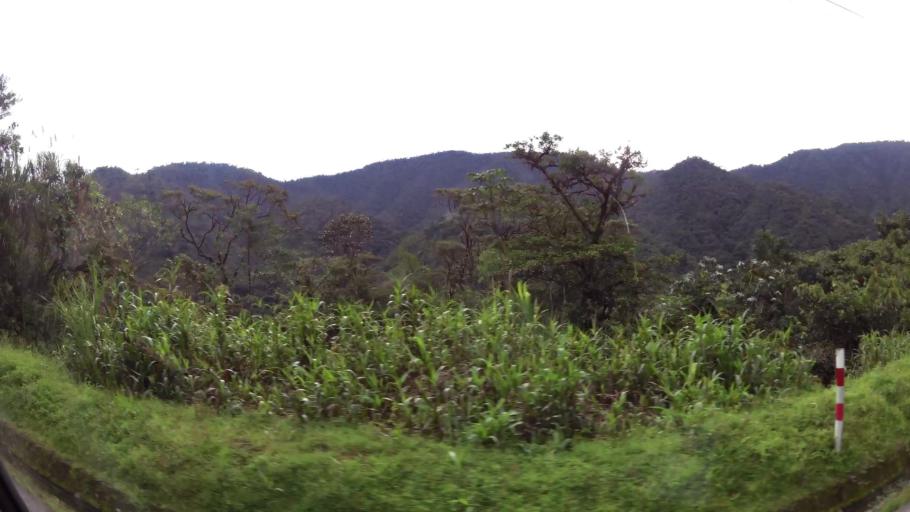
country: EC
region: Pastaza
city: Puyo
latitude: -1.4410
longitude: -78.1790
